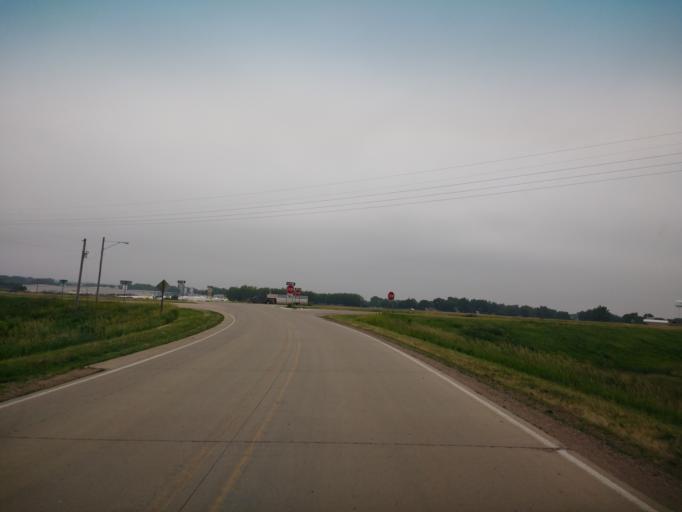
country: US
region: Iowa
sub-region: O'Brien County
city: Sheldon
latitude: 43.0615
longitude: -95.8999
